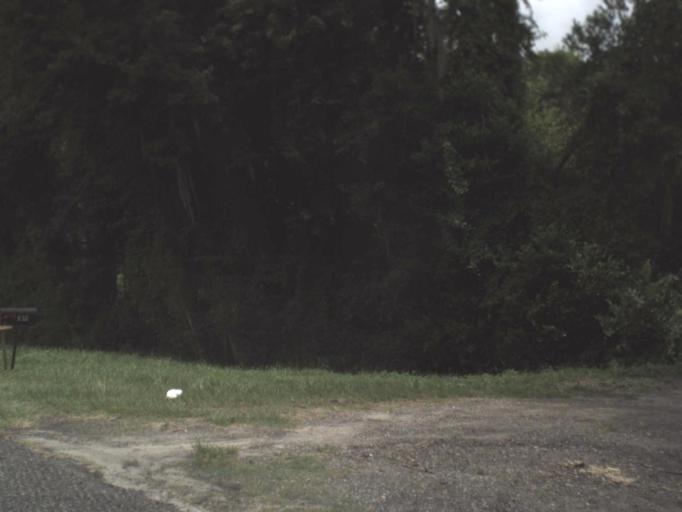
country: US
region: Florida
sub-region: Columbia County
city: Lake City
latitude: 30.1593
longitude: -82.6427
